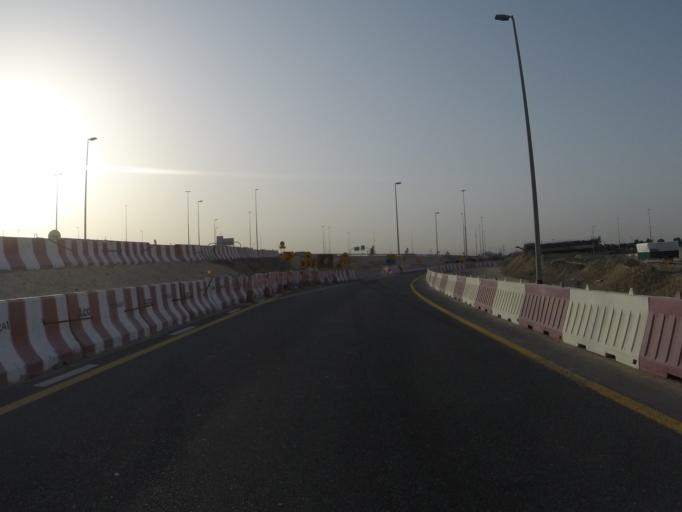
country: AE
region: Dubai
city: Dubai
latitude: 25.1695
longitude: 55.2651
